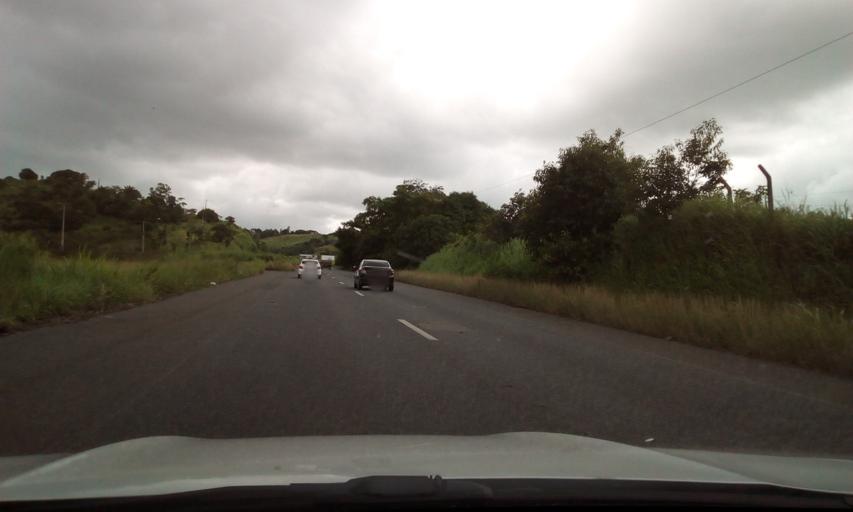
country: BR
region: Pernambuco
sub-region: Moreno
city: Moreno
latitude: -8.1108
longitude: -35.1498
